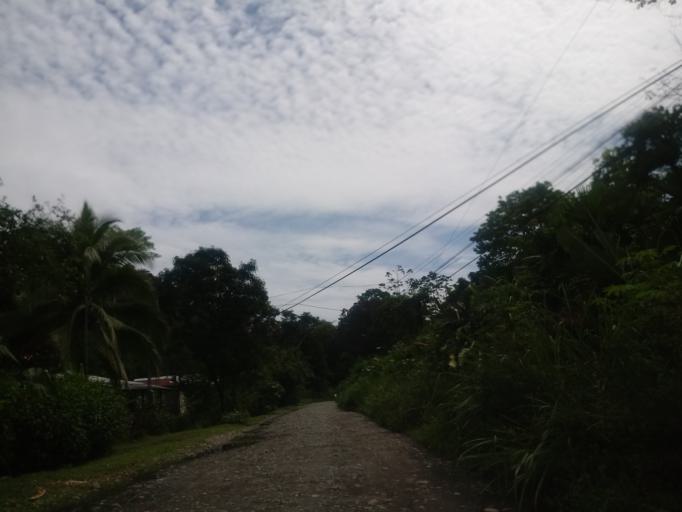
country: CR
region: Limon
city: Limon
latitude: 9.7535
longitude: -82.8811
